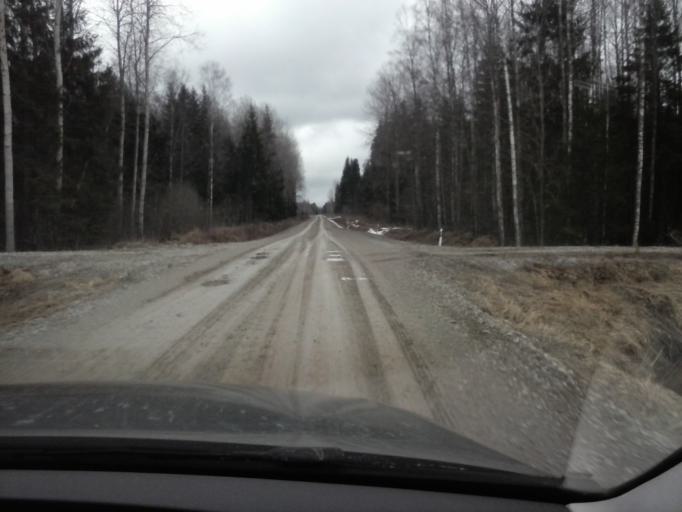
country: EE
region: Jogevamaa
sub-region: Mustvee linn
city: Mustvee
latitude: 59.0589
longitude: 26.8259
